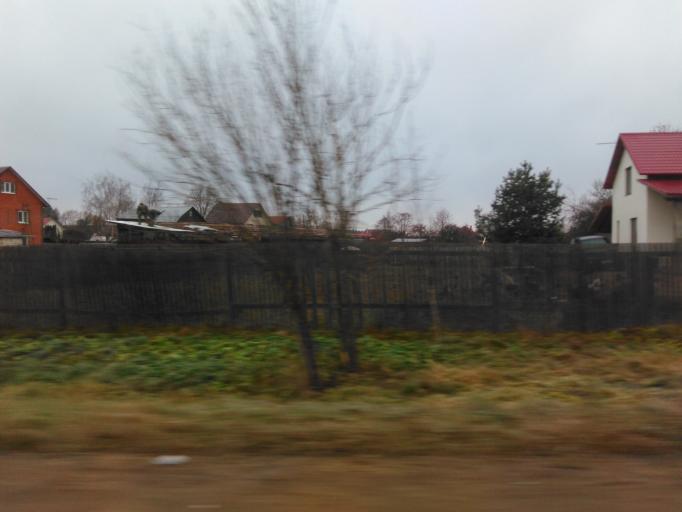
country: RU
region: Moskovskaya
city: Ashukino
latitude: 56.1748
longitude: 37.9389
